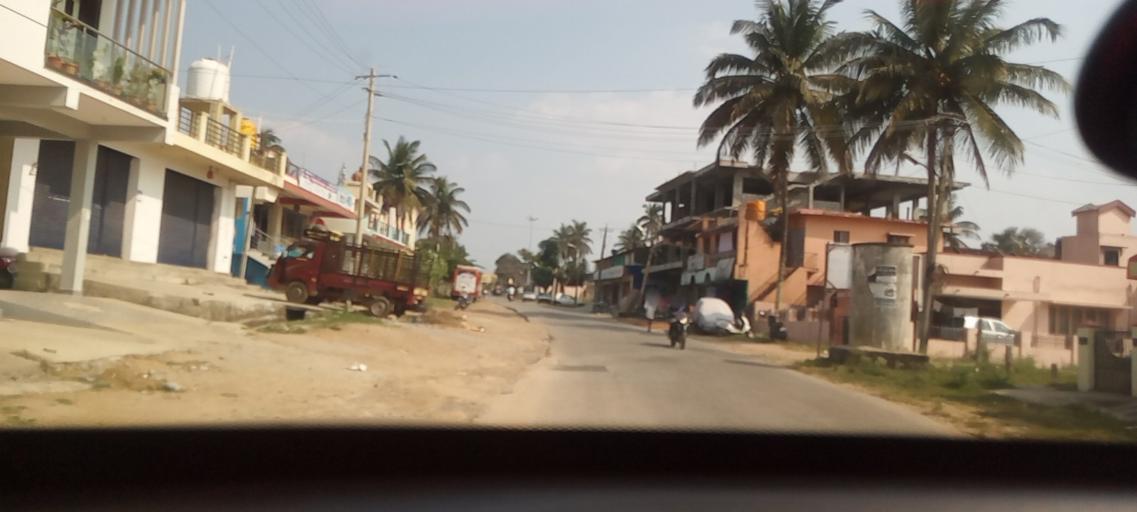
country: IN
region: Karnataka
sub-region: Hassan
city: Belur
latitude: 13.1674
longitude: 75.8611
